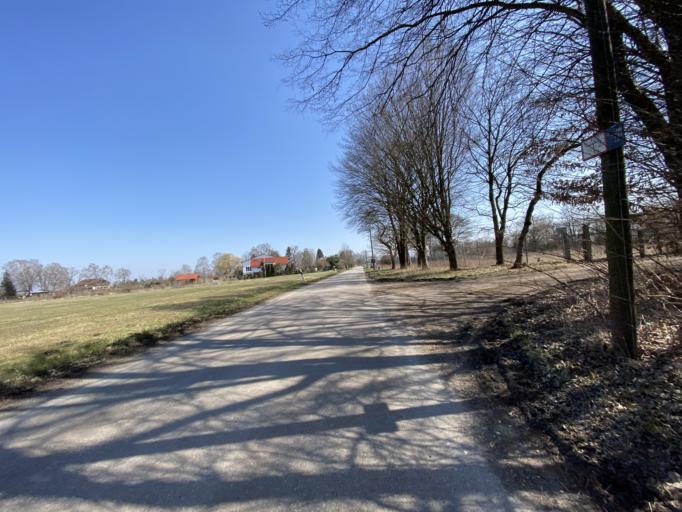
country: DE
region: Bavaria
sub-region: Upper Bavaria
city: Unterfoehring
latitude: 48.1717
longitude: 11.6693
